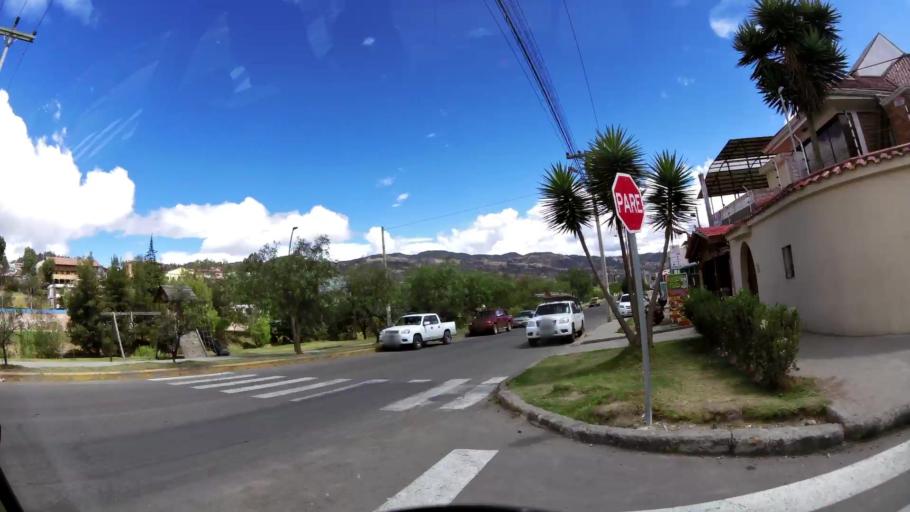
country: EC
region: Canar
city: Azogues
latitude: -2.7451
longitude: -78.8500
